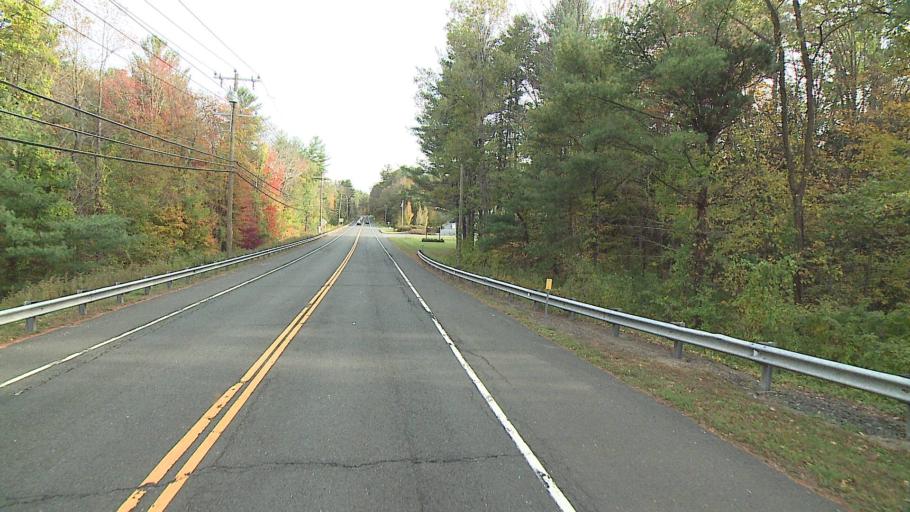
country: US
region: Connecticut
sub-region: Litchfield County
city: New Hartford Center
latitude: 41.8968
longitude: -72.9898
